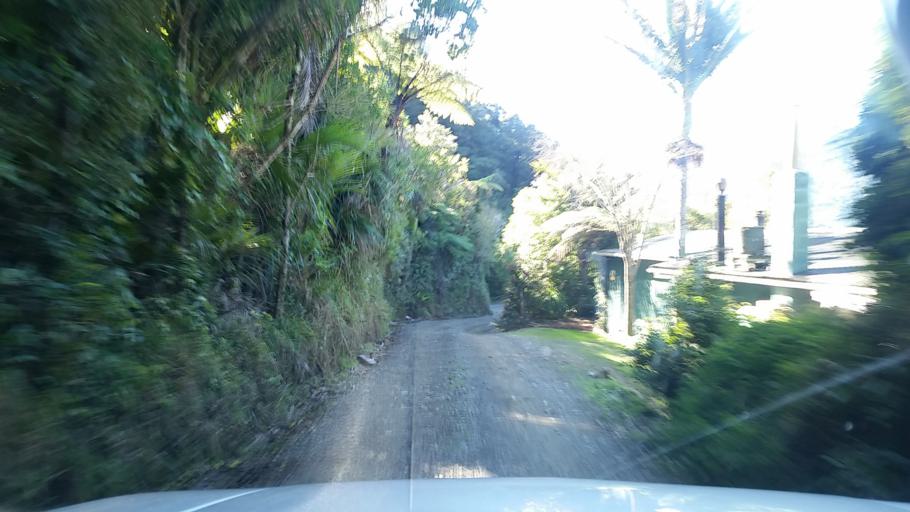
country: NZ
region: Marlborough
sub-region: Marlborough District
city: Picton
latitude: -41.1049
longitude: 173.6550
